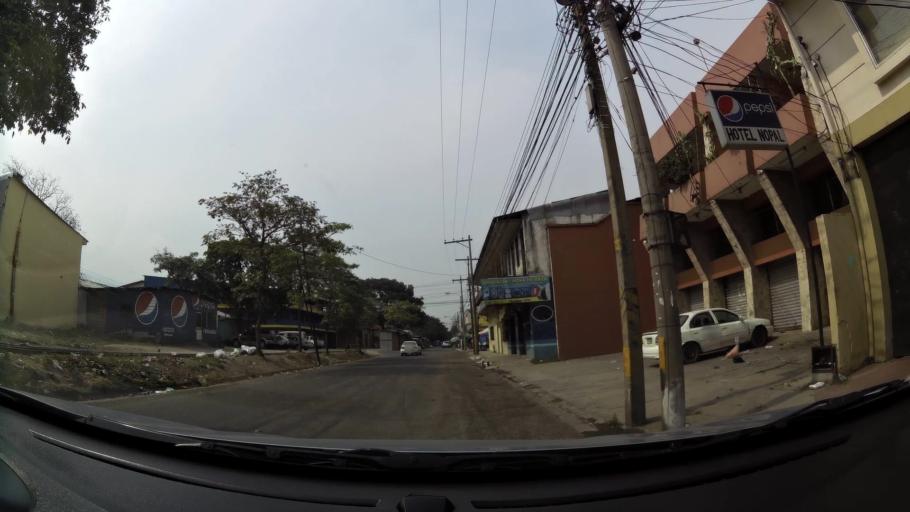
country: HN
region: Cortes
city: San Pedro Sula
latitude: 15.4980
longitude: -88.0239
